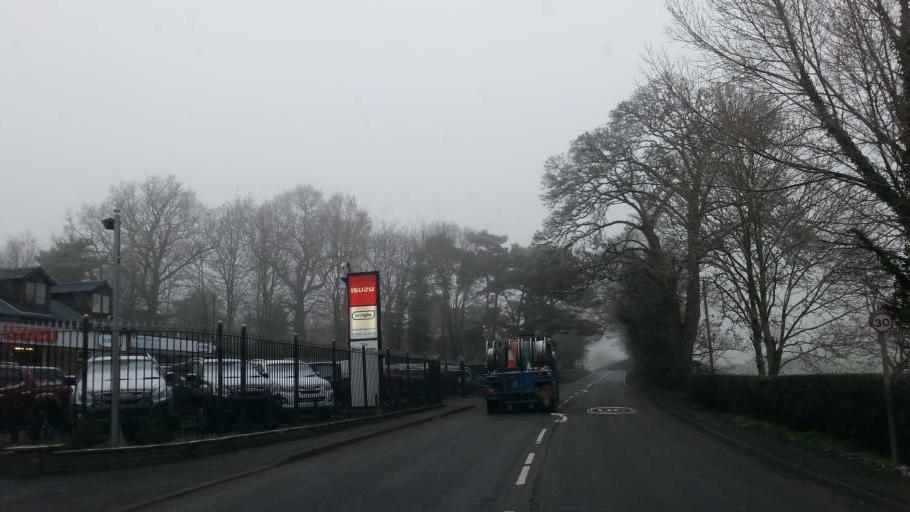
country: GB
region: England
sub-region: Cheshire East
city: Siddington
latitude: 53.2129
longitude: -2.2287
